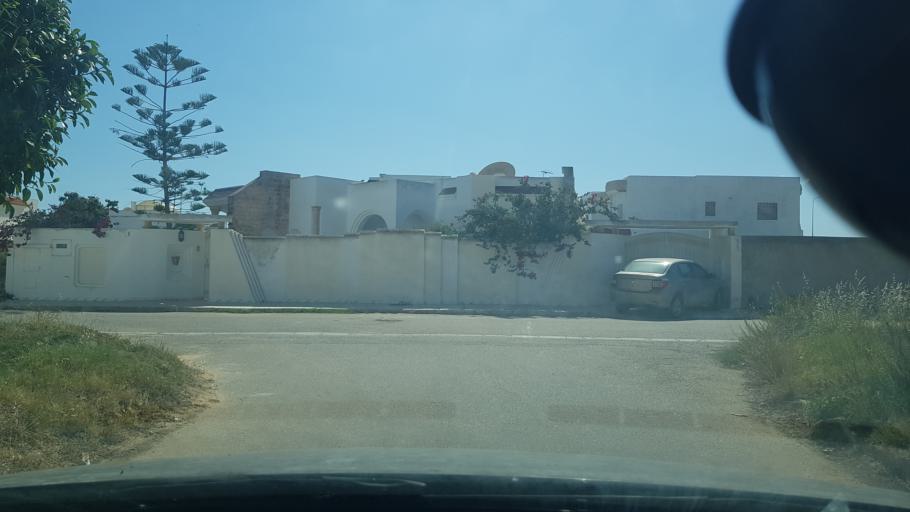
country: TN
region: Safaqis
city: Al Qarmadah
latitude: 34.8310
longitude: 10.7575
